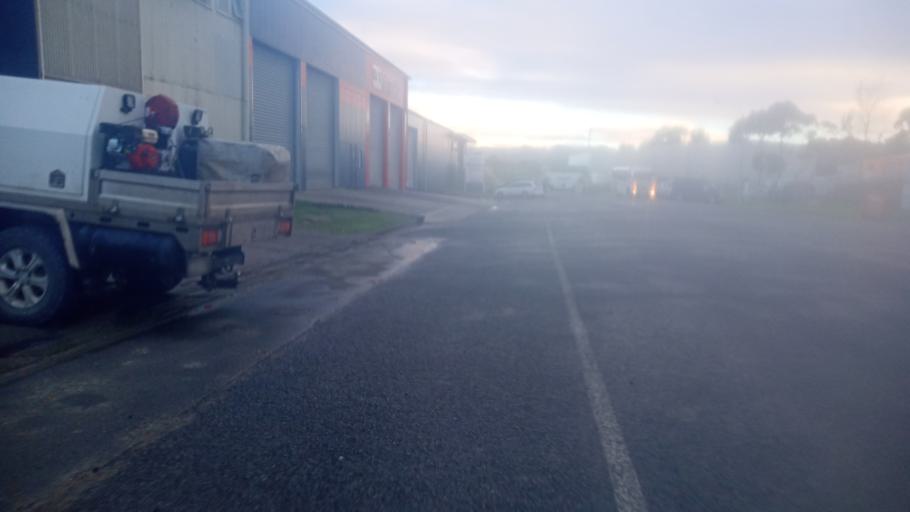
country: NZ
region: Gisborne
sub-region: Gisborne District
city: Gisborne
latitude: -38.6665
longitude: 178.0018
